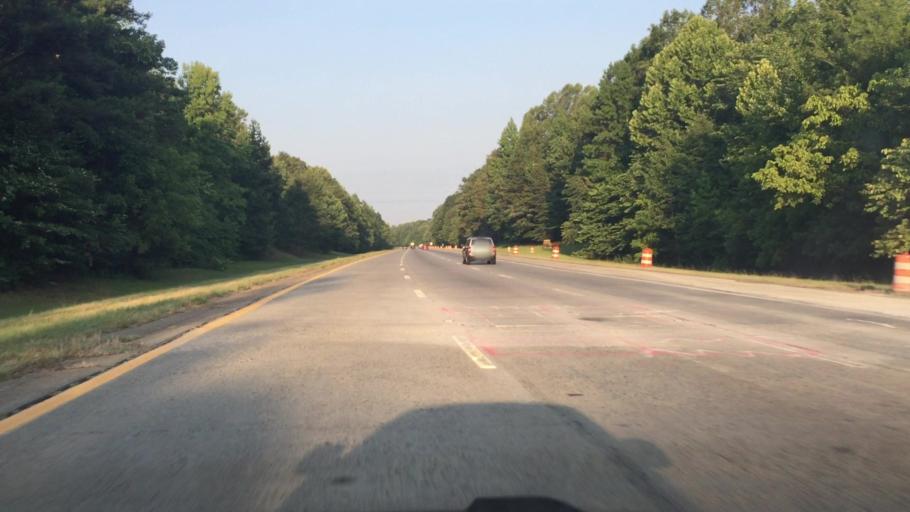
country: US
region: North Carolina
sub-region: Davidson County
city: Thomasville
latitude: 35.8352
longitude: -80.1367
